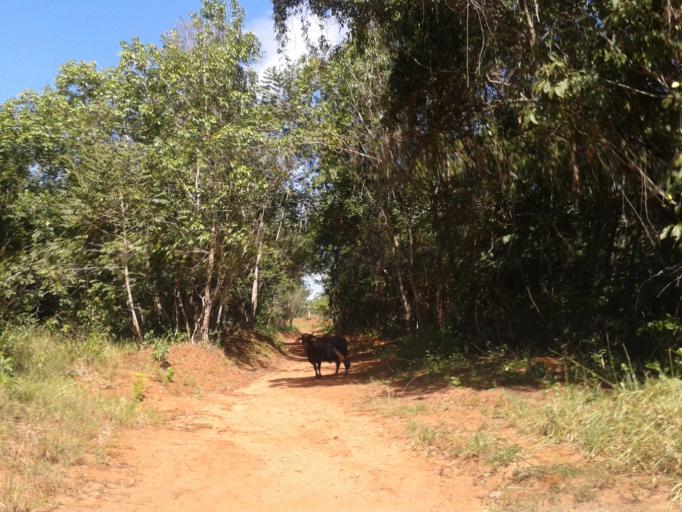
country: BR
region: Minas Gerais
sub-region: Campina Verde
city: Campina Verde
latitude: -19.3945
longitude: -49.7411
